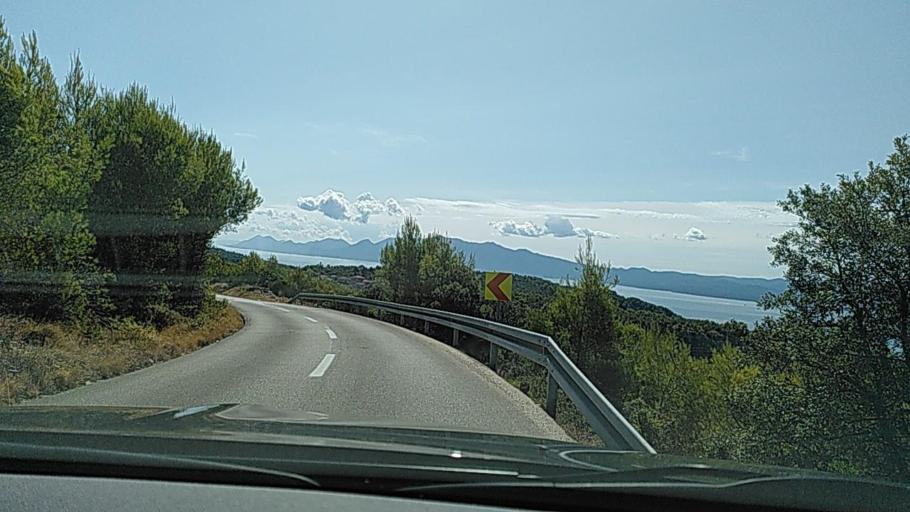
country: HR
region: Splitsko-Dalmatinska
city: Tucepi
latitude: 43.1340
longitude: 16.9764
